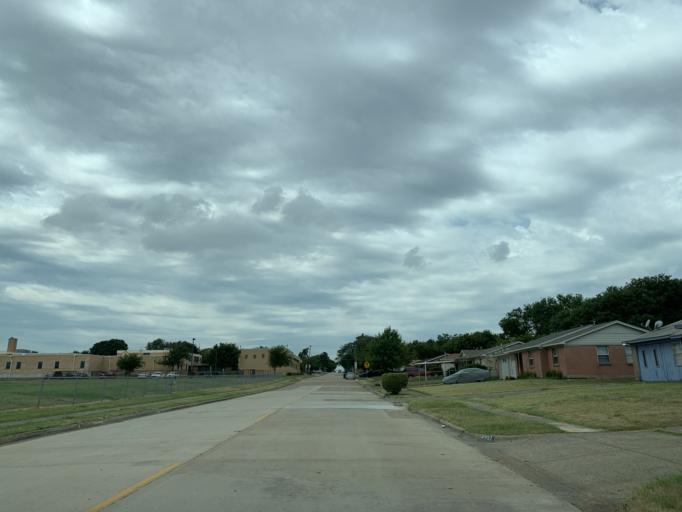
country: US
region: Texas
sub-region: Dallas County
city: DeSoto
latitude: 32.6539
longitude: -96.8335
